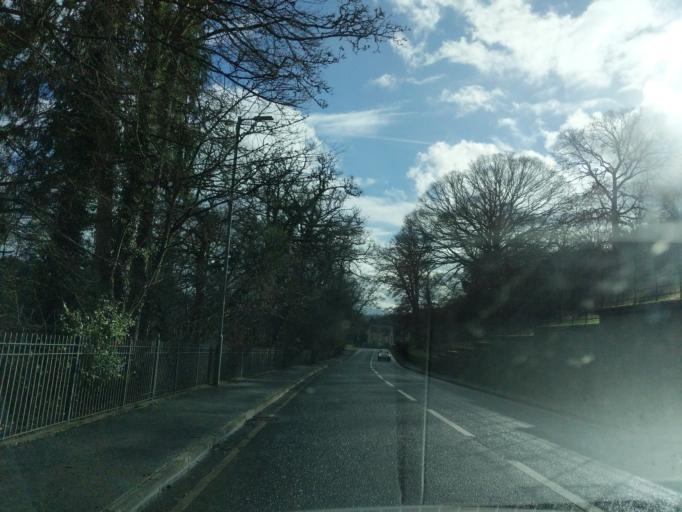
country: GB
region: Scotland
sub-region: South Lanarkshire
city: Carluke
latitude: 55.6950
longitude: -3.8666
